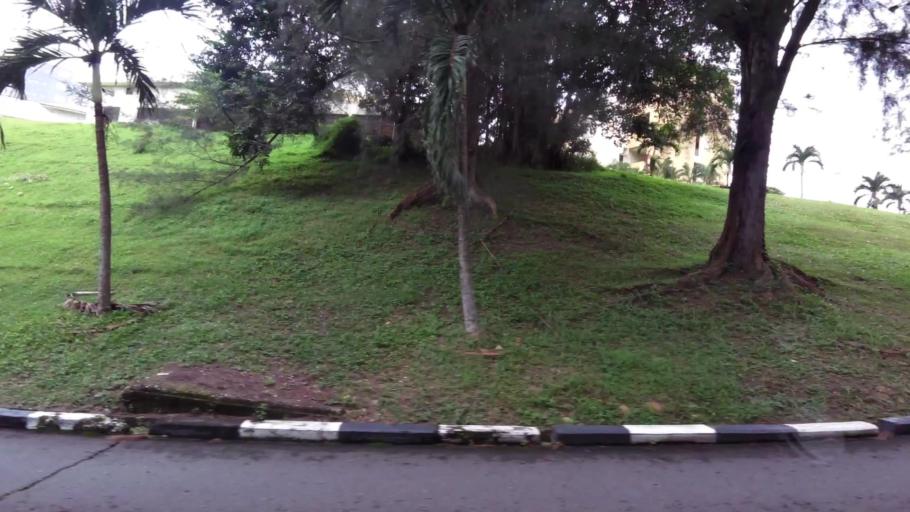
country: BN
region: Brunei and Muara
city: Bandar Seri Begawan
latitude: 4.8916
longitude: 114.9331
